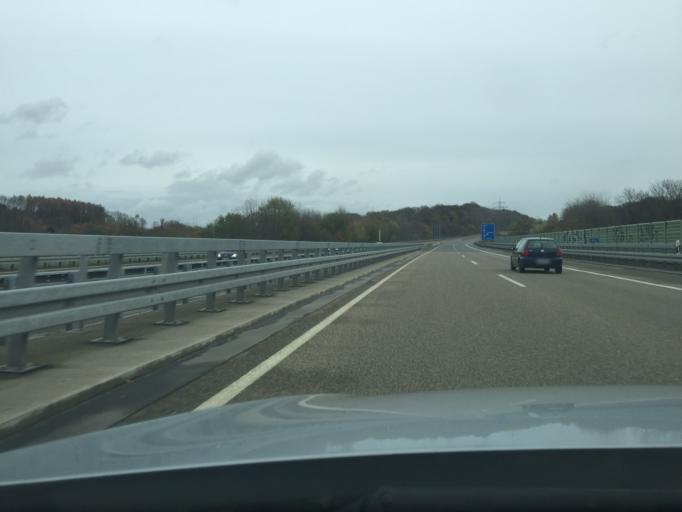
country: DE
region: North Rhine-Westphalia
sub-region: Regierungsbezirk Dusseldorf
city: Velbert
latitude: 51.3599
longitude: 7.0546
